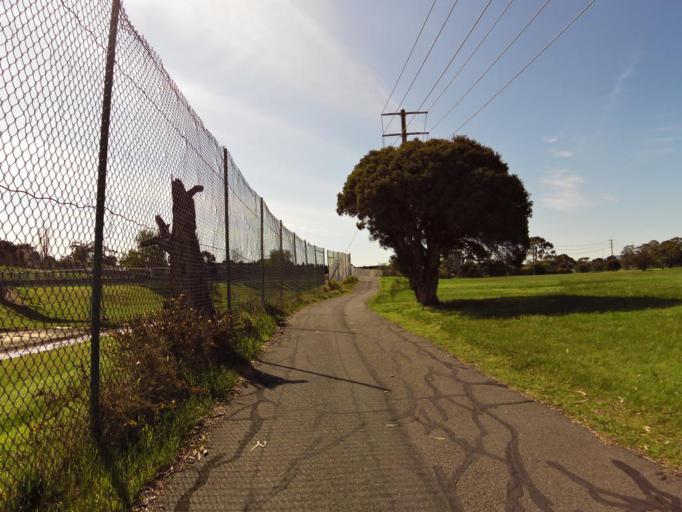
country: AU
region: Victoria
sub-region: Casey
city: Doveton
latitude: -37.9918
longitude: 145.2275
